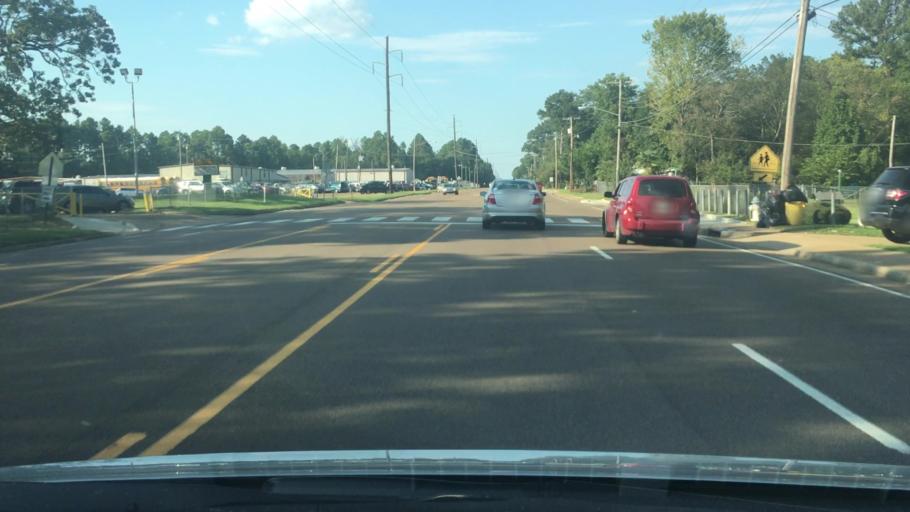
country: US
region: Mississippi
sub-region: Hinds County
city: Jackson
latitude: 32.3568
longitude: -90.1927
